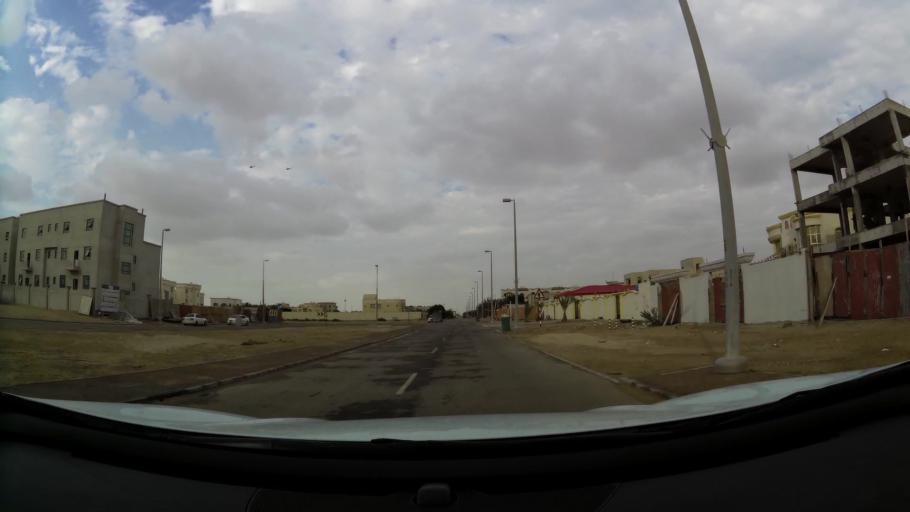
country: AE
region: Abu Dhabi
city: Abu Dhabi
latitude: 24.3507
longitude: 54.6133
